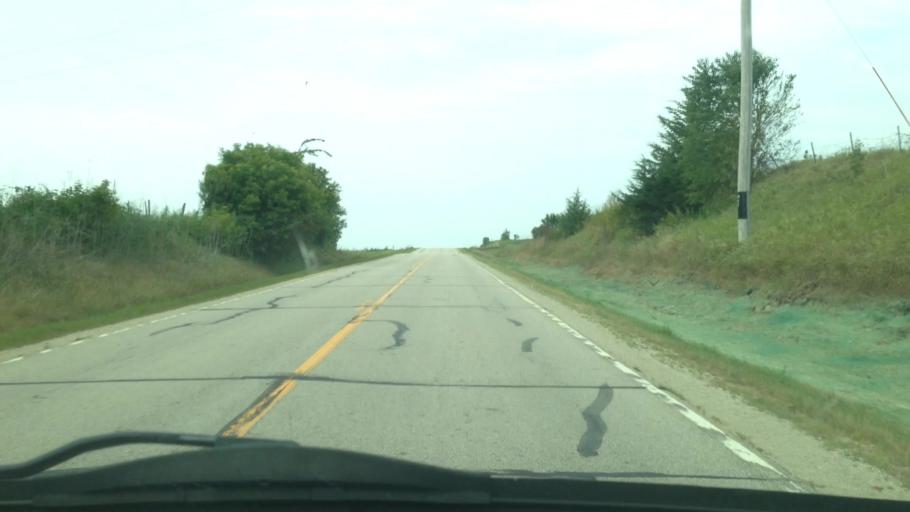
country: US
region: Minnesota
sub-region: Fillmore County
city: Preston
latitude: 43.7717
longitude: -91.9498
